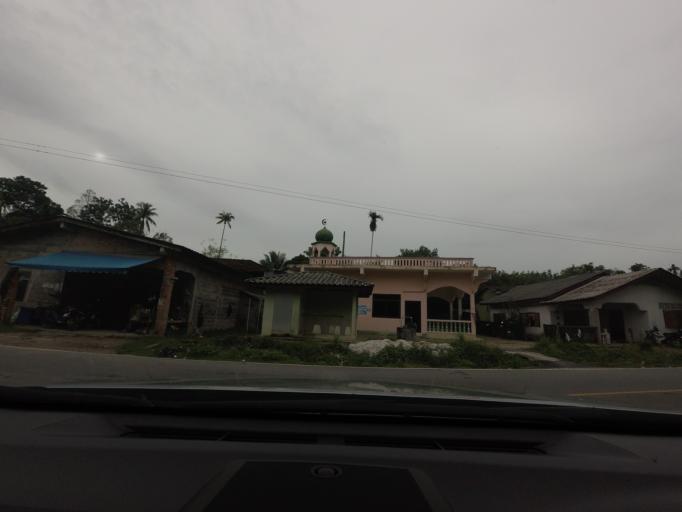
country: TH
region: Narathiwat
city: Rueso
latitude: 6.4152
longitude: 101.5263
